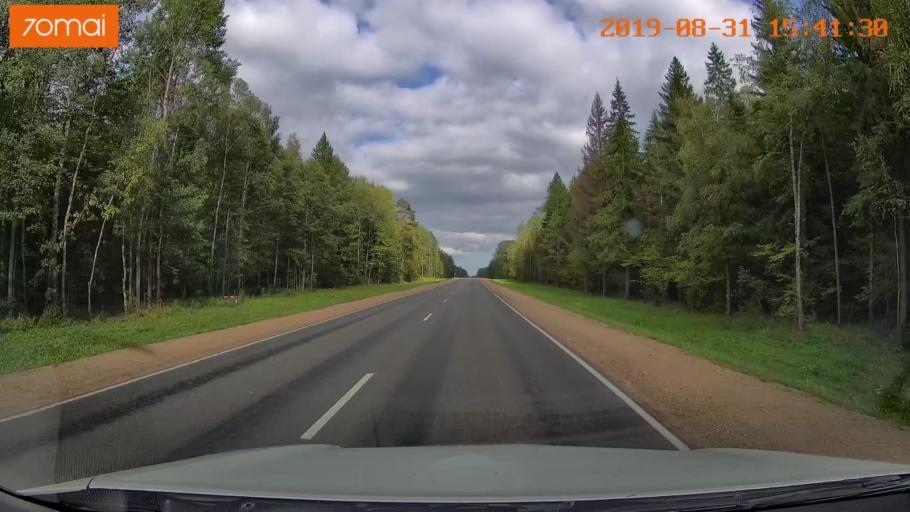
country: RU
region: Kaluga
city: Mosal'sk
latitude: 54.6396
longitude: 34.8620
